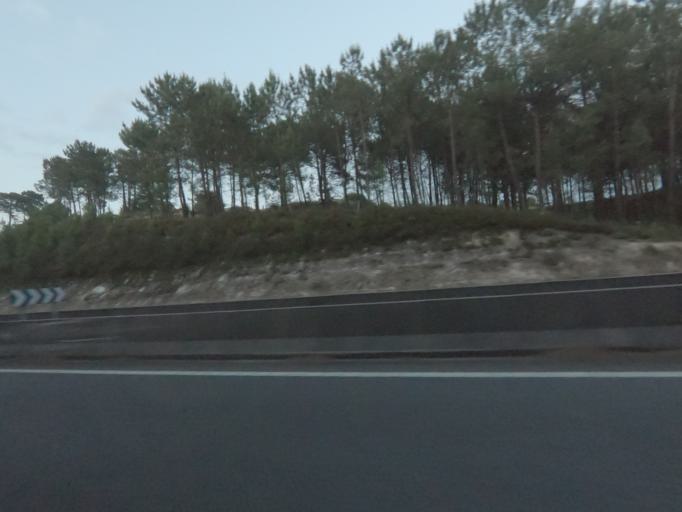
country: ES
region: Galicia
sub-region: Provincia de Pontevedra
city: Tui
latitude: 42.0776
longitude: -8.6330
